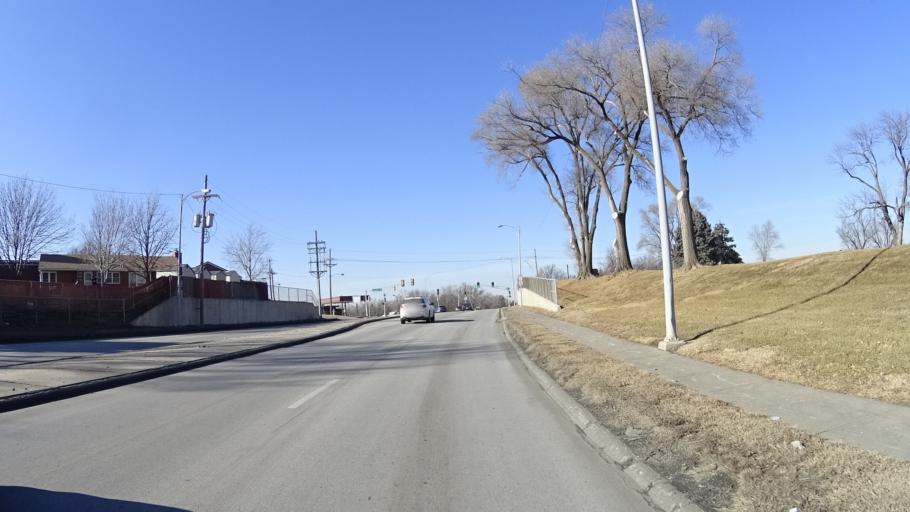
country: US
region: Nebraska
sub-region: Douglas County
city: Ralston
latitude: 41.3020
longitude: -96.0323
